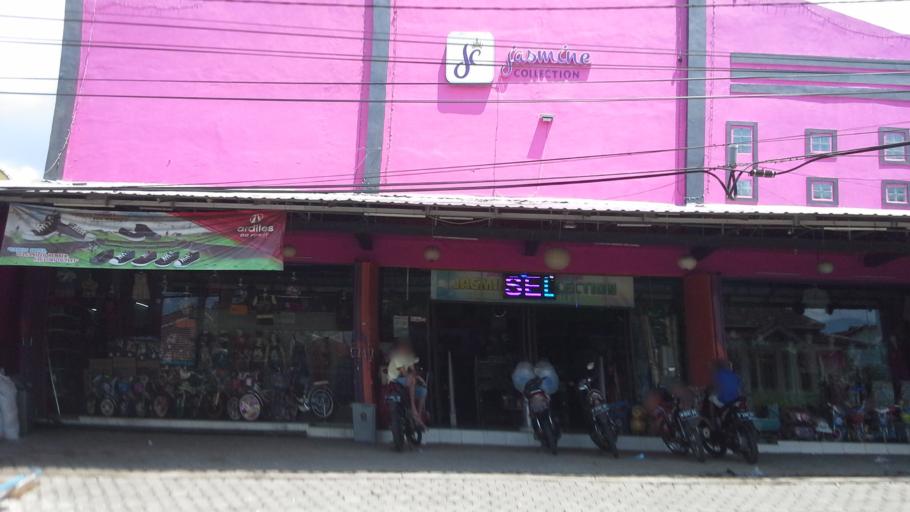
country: ID
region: East Java
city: Maesan
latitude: -8.0272
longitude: 113.7767
